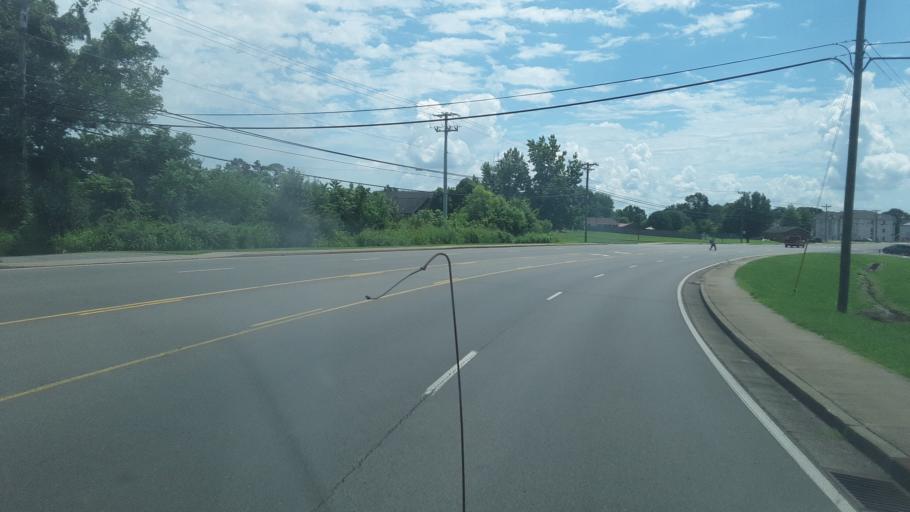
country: US
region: Kentucky
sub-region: Christian County
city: Fort Campbell North
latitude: 36.5757
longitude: -87.4330
